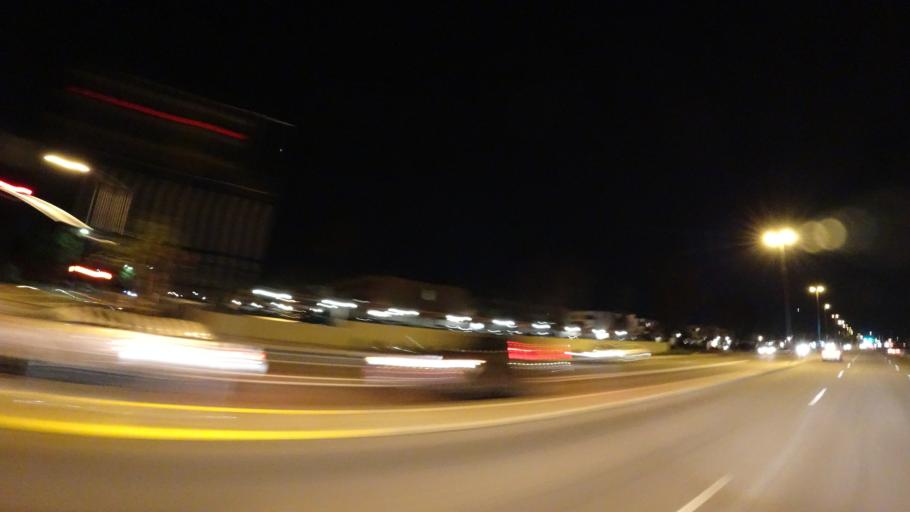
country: US
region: Arizona
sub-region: Maricopa County
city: San Carlos
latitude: 33.3787
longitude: -111.8690
